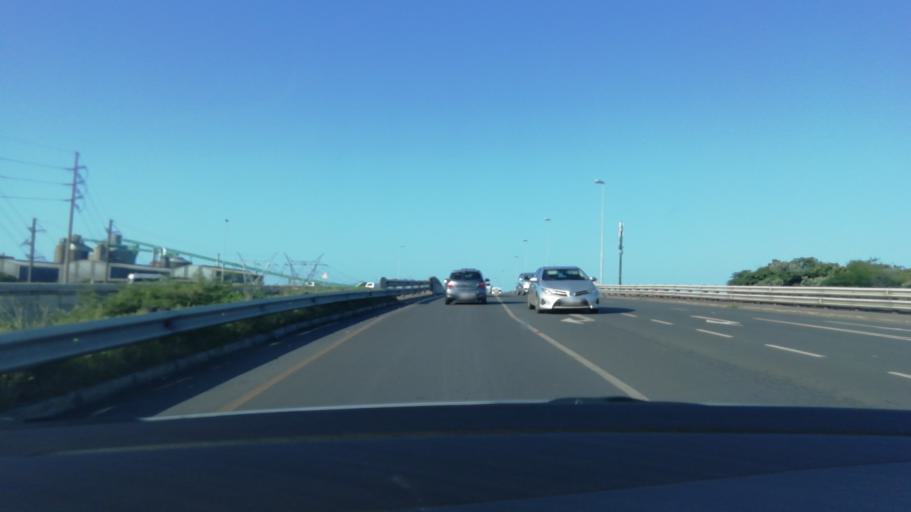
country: ZA
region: KwaZulu-Natal
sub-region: uThungulu District Municipality
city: Richards Bay
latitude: -28.7714
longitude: 32.0338
